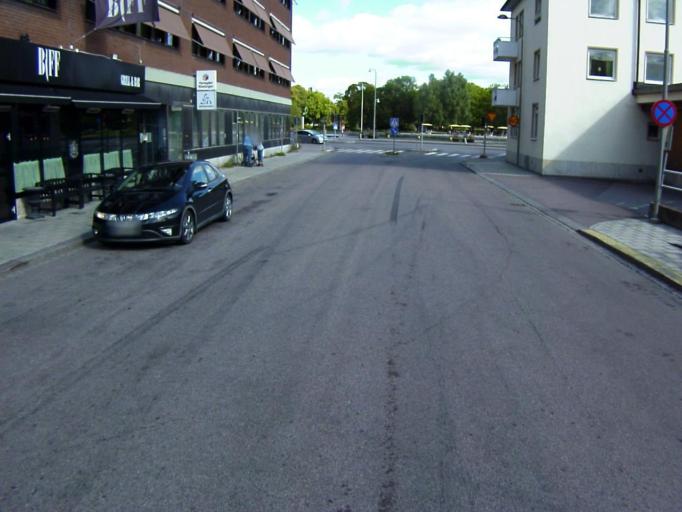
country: SE
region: Soedermanland
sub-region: Eskilstuna Kommun
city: Eskilstuna
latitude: 59.3705
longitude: 16.5158
